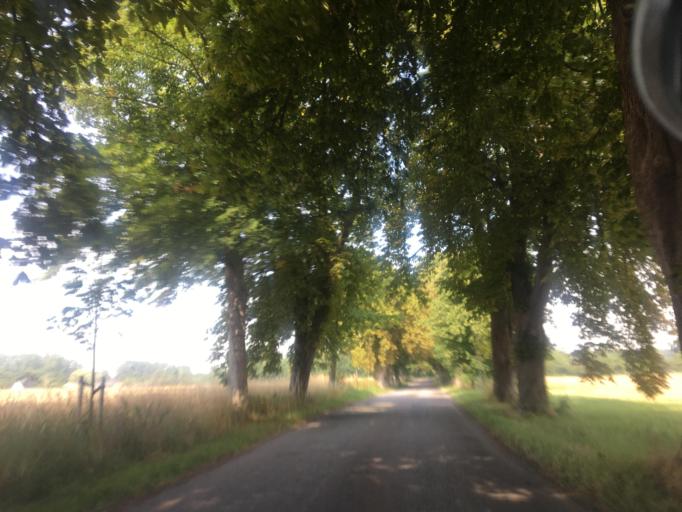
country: DK
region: Zealand
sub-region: Vordingborg Kommune
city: Praesto
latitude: 55.1848
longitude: 12.0754
